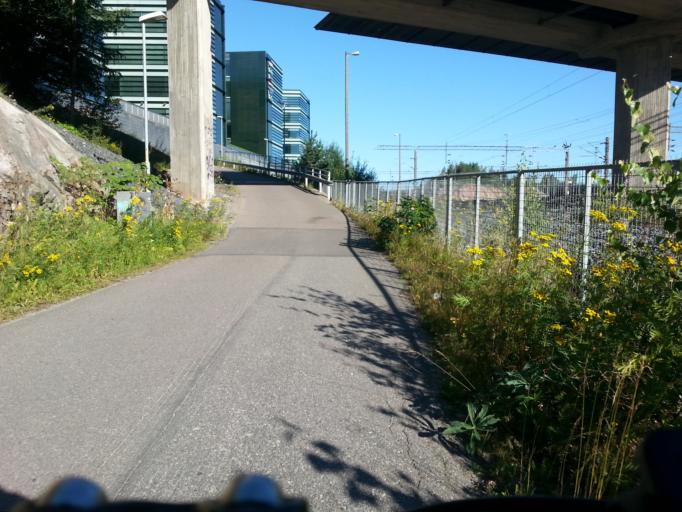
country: FI
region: Uusimaa
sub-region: Helsinki
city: Helsinki
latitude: 60.2044
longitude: 24.9271
